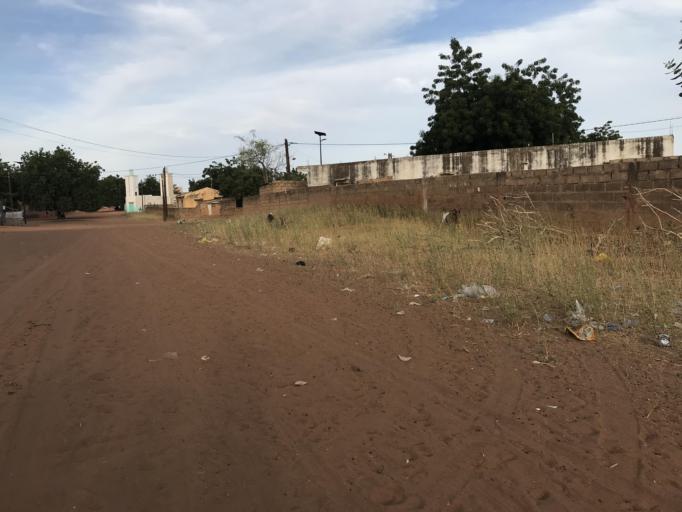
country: SN
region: Louga
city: Ndibene Dahra
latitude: 15.3981
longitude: -15.1187
